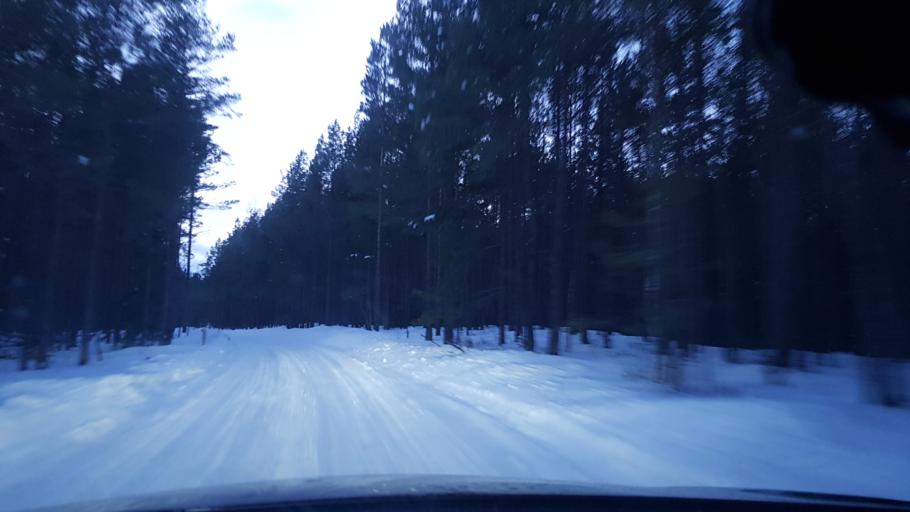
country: EE
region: Laeaene
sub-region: Haapsalu linn
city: Haapsalu
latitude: 59.2117
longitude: 23.5651
